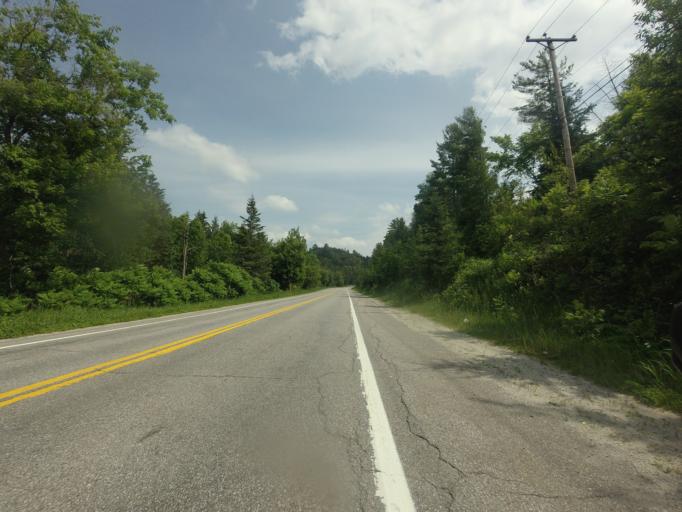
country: CA
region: Quebec
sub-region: Outaouais
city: Wakefield
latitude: 45.7667
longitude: -75.9336
